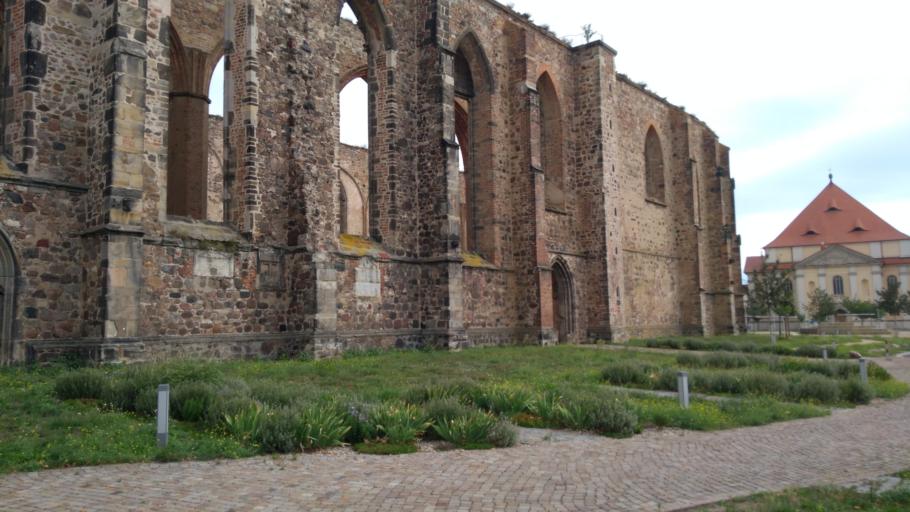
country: DE
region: Saxony-Anhalt
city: Zerbst
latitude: 51.9690
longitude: 12.0846
